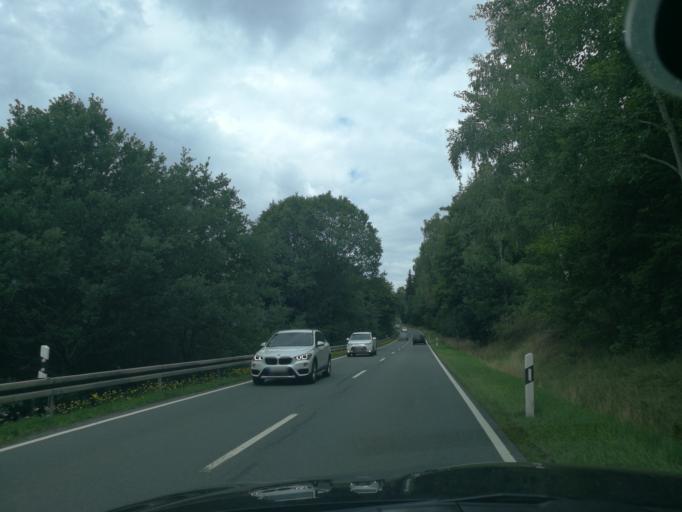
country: DE
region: Saxony
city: Adorf
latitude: 50.3585
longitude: 12.2260
